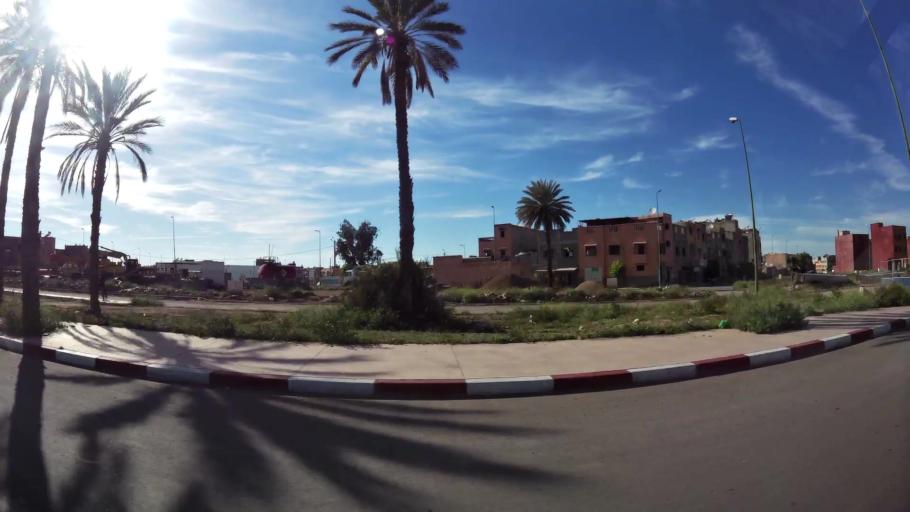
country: MA
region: Marrakech-Tensift-Al Haouz
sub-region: Marrakech
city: Marrakesh
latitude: 31.6761
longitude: -8.0583
